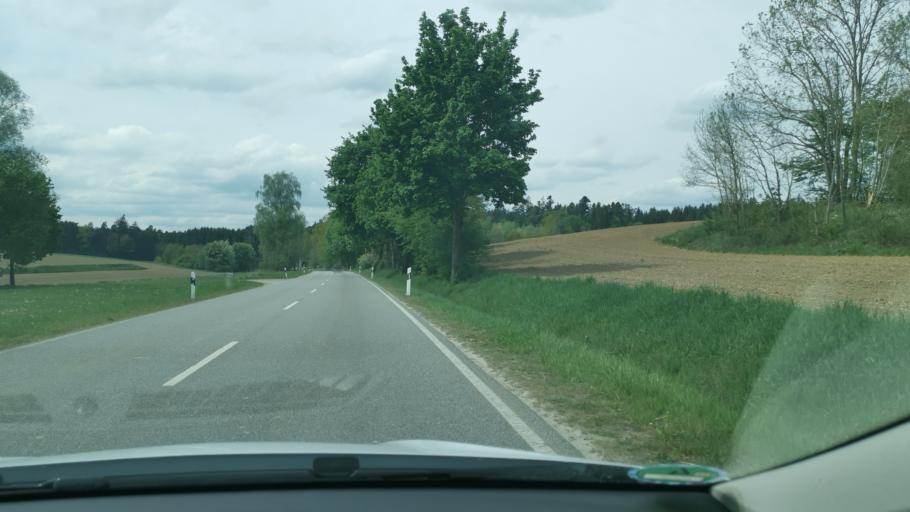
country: DE
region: Bavaria
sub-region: Upper Bavaria
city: Petershausen
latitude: 48.4137
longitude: 11.4608
